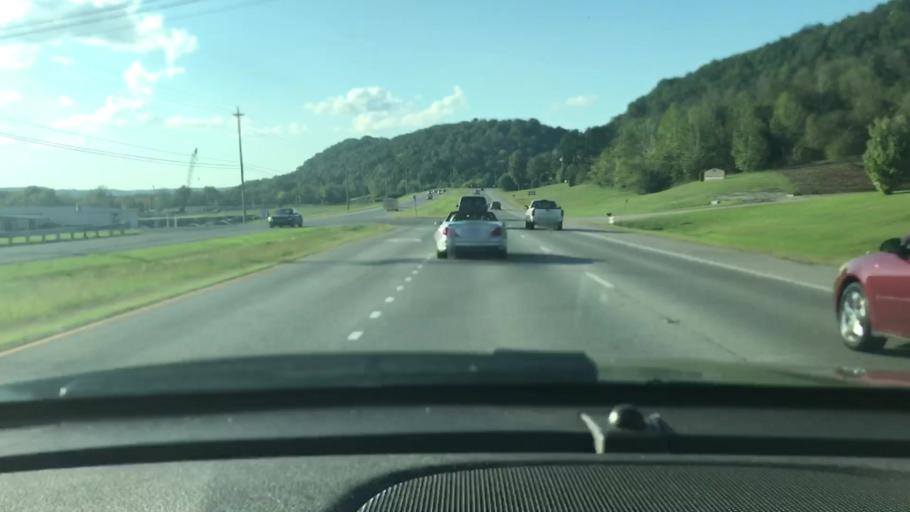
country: US
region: Tennessee
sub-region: Cheatham County
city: Ashland City
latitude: 36.2285
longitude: -87.0131
